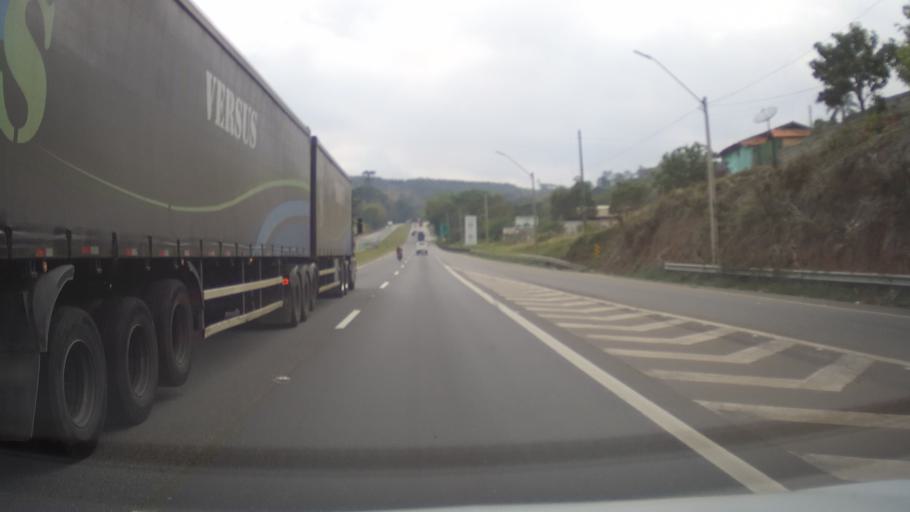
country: BR
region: Minas Gerais
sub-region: Extrema
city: Extrema
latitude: -22.8814
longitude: -46.4048
